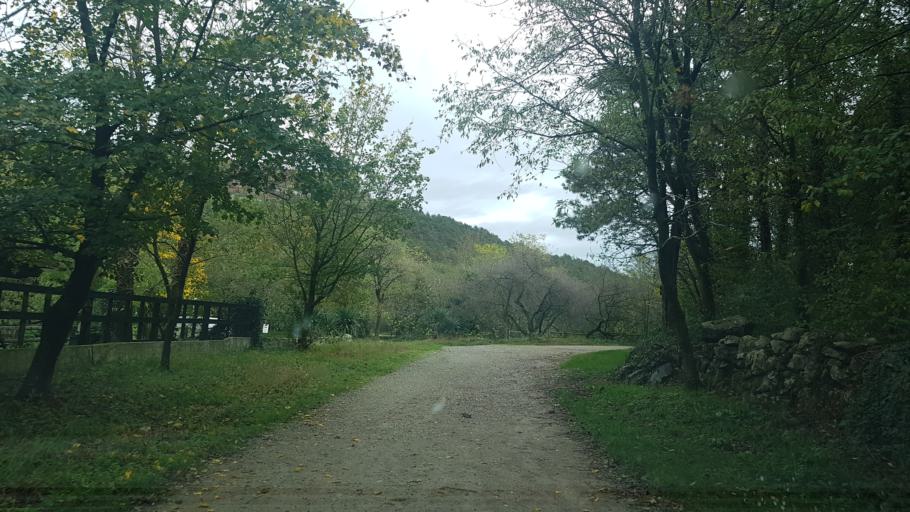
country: IT
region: Friuli Venezia Giulia
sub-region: Provincia di Gorizia
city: Monfalcone
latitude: 45.8172
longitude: 13.5359
